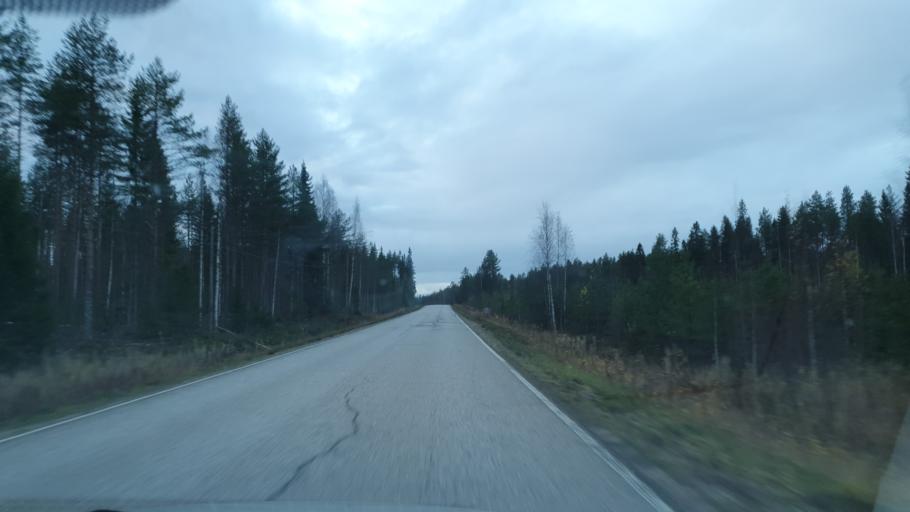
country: FI
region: Kainuu
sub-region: Kajaani
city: Ristijaervi
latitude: 64.4232
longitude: 28.4006
